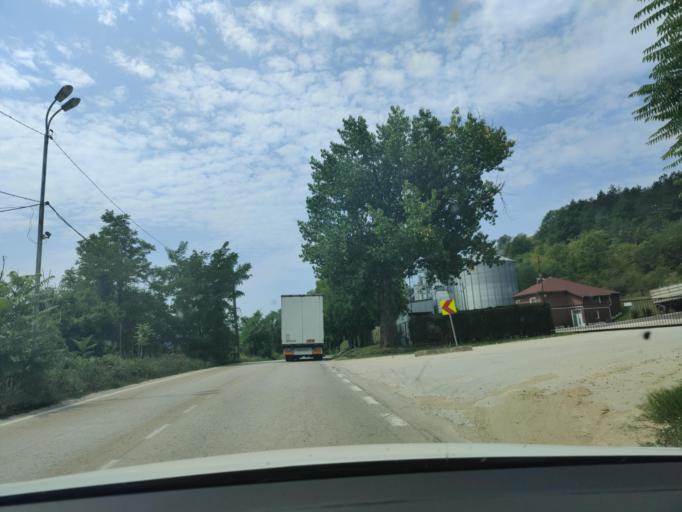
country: BG
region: Vidin
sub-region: Obshtina Dimovo
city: Dimovo
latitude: 43.7500
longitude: 22.7373
